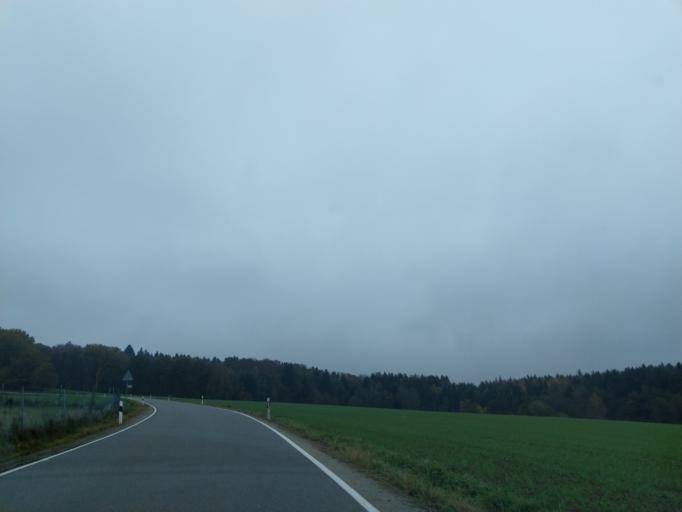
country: DE
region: Bavaria
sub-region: Lower Bavaria
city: Auerbach
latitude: 48.7868
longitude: 13.1134
